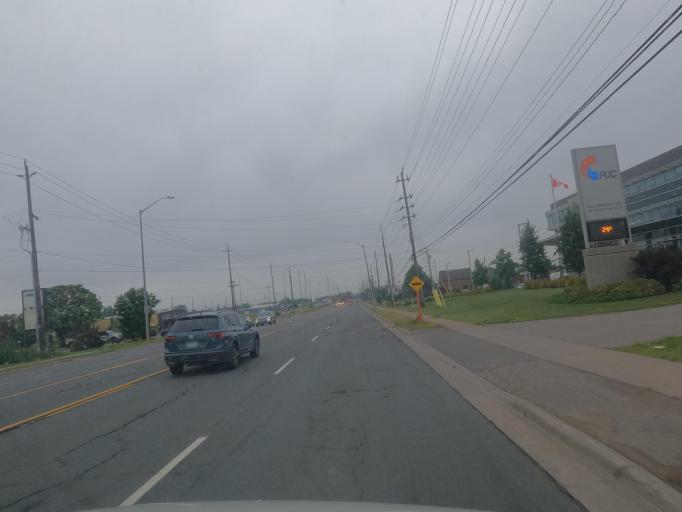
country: CA
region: Ontario
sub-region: Algoma
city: Sault Ste. Marie
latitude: 46.5384
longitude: -84.3256
